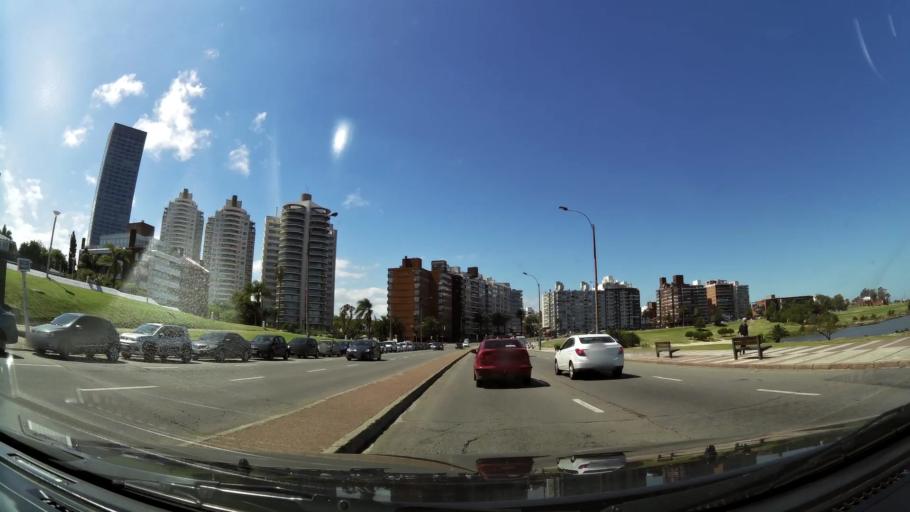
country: UY
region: Montevideo
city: Montevideo
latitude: -34.9065
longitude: -56.1332
